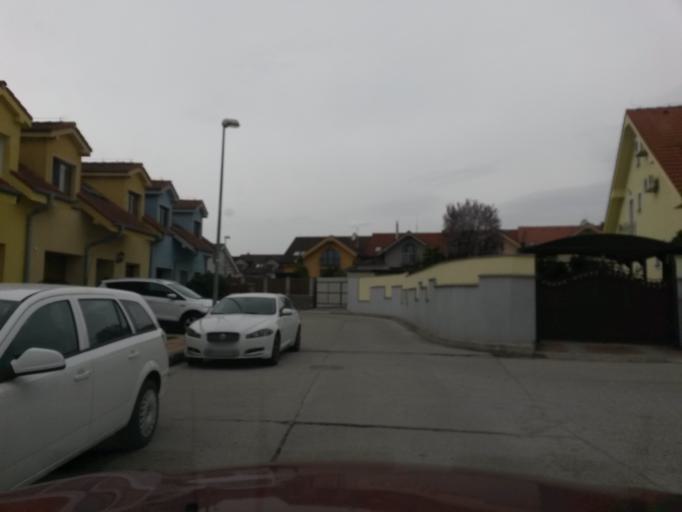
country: SK
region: Kosicky
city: Kosice
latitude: 48.7028
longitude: 21.2259
